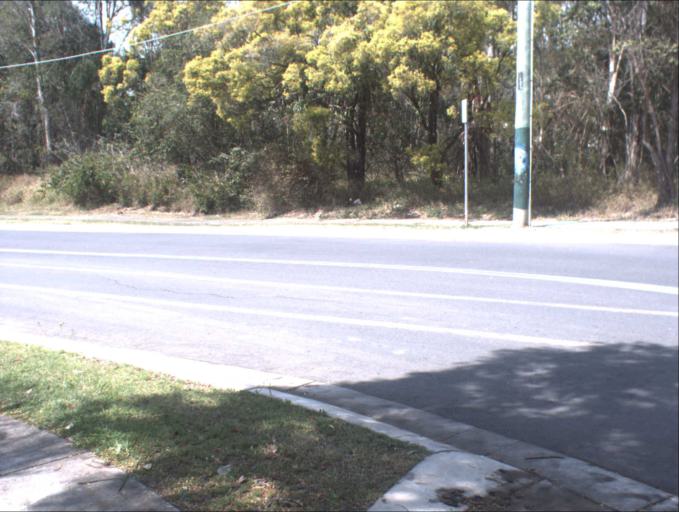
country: AU
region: Queensland
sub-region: Logan
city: Slacks Creek
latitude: -27.6480
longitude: 153.1571
